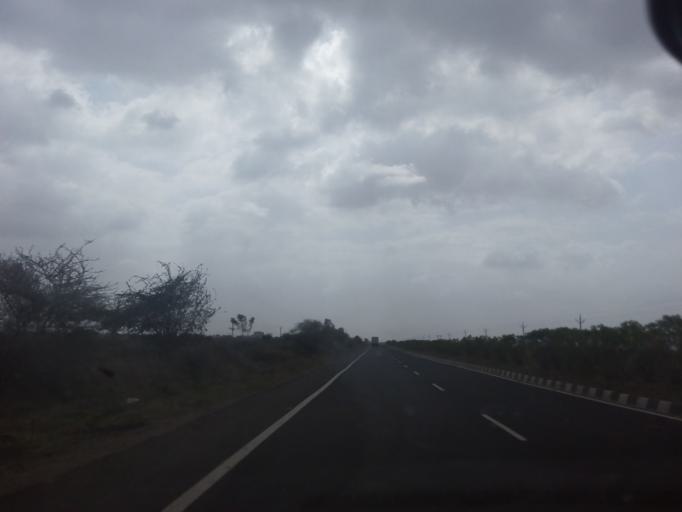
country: IN
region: Gujarat
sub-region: Surendranagar
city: Halvad
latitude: 23.0051
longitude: 71.1327
